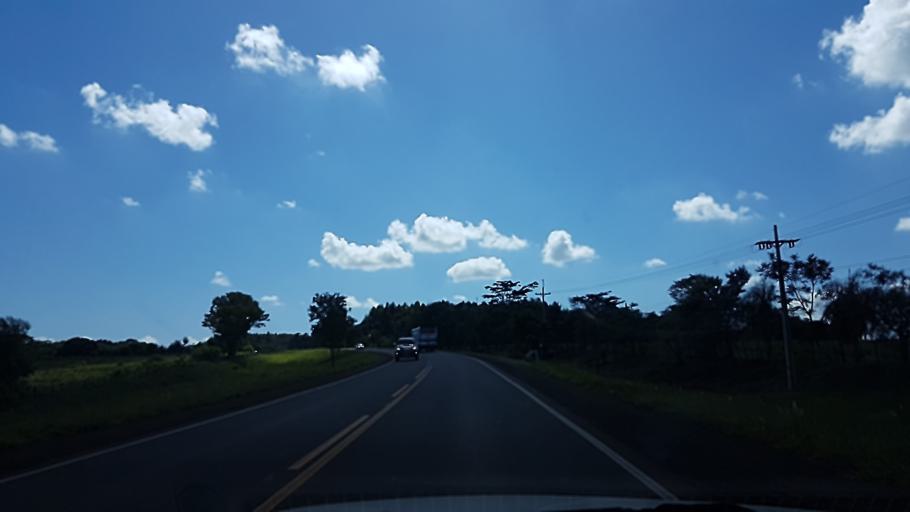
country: PY
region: Itapua
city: Carmen del Parana
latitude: -27.2204
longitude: -56.1021
